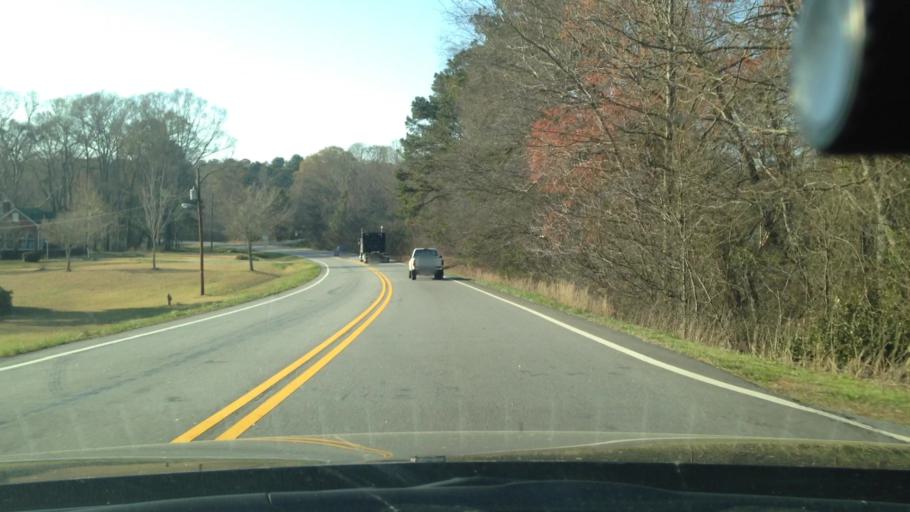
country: US
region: Georgia
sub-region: Fayette County
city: Peachtree City
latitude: 33.3369
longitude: -84.6503
